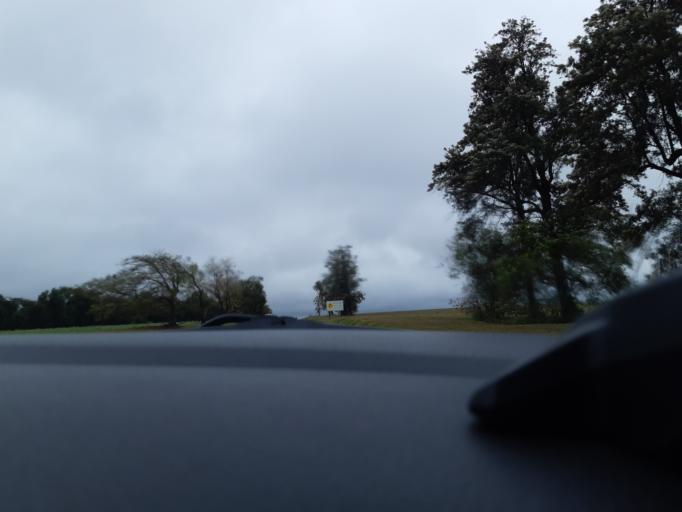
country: BR
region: Sao Paulo
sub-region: Ourinhos
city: Ourinhos
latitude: -23.0013
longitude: -49.9439
